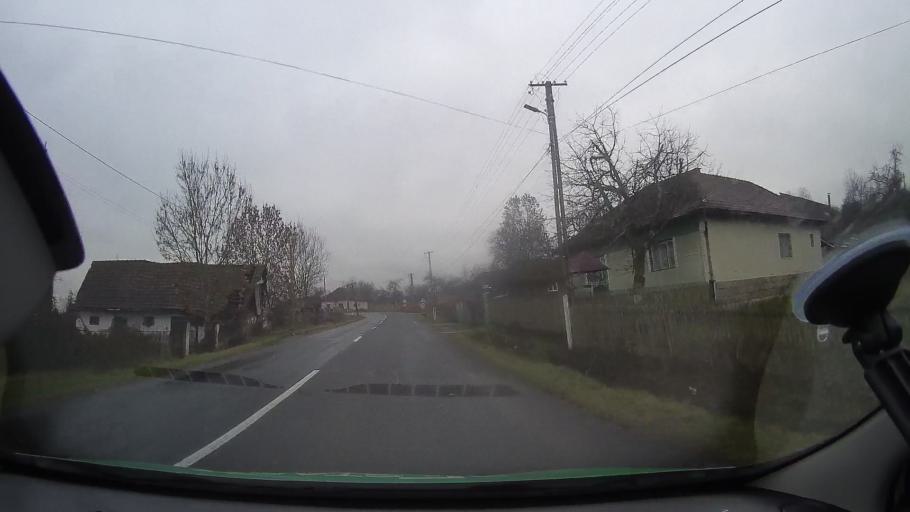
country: RO
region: Arad
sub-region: Comuna Varfurile
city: Varfurile
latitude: 46.3179
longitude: 22.5086
